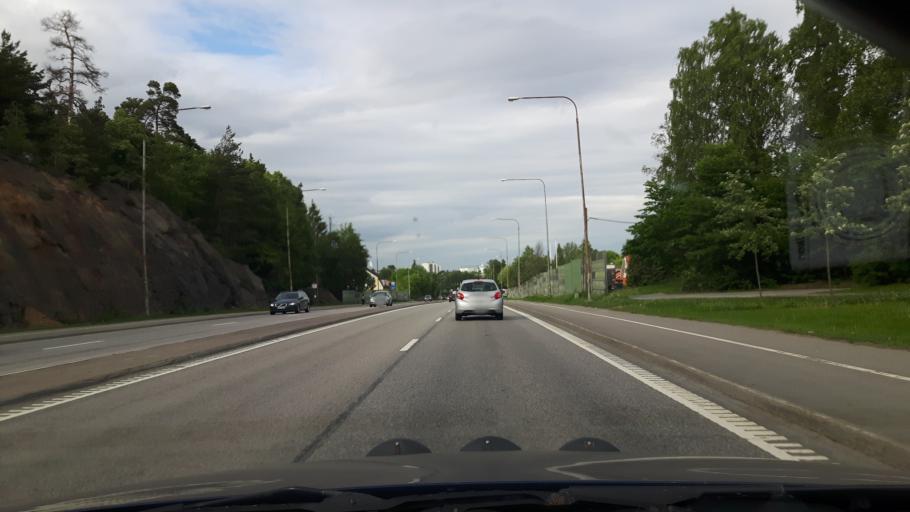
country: SE
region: Stockholm
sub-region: Huddinge Kommun
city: Huddinge
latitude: 59.2469
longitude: 18.0032
